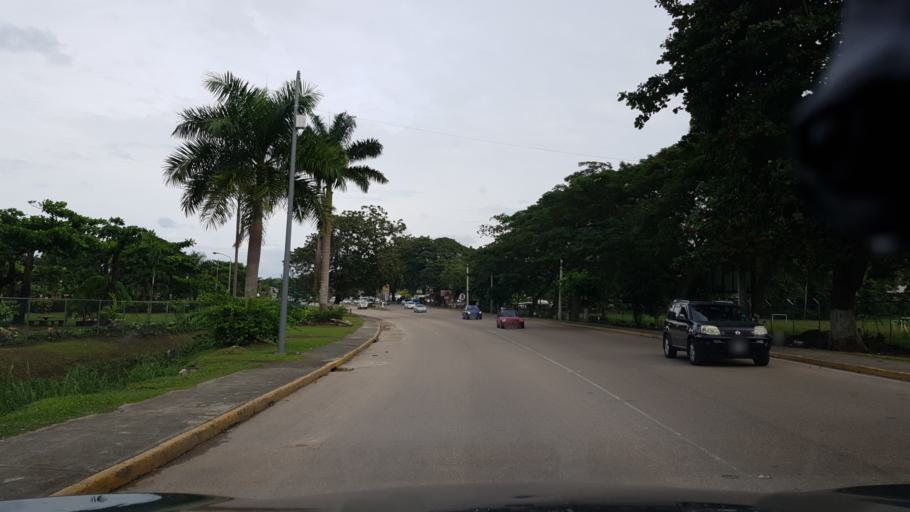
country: JM
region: Saint Ann
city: Ocho Rios
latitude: 18.4048
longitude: -77.1076
